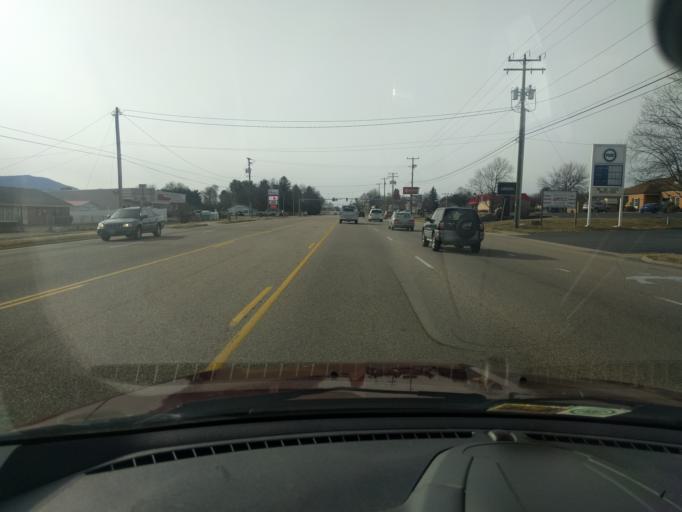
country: US
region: Virginia
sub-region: Augusta County
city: Stuarts Draft
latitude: 38.0341
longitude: -79.0367
